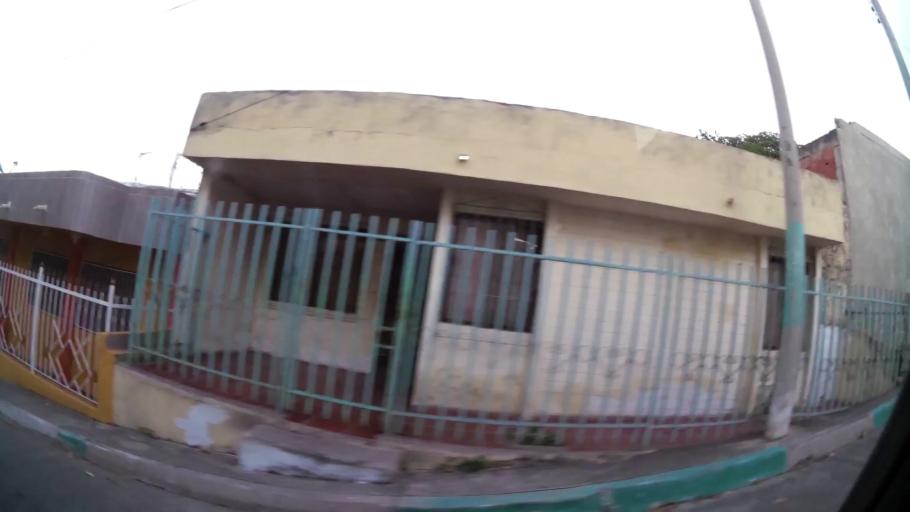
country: CO
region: Bolivar
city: Cartagena
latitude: 10.4004
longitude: -75.5141
